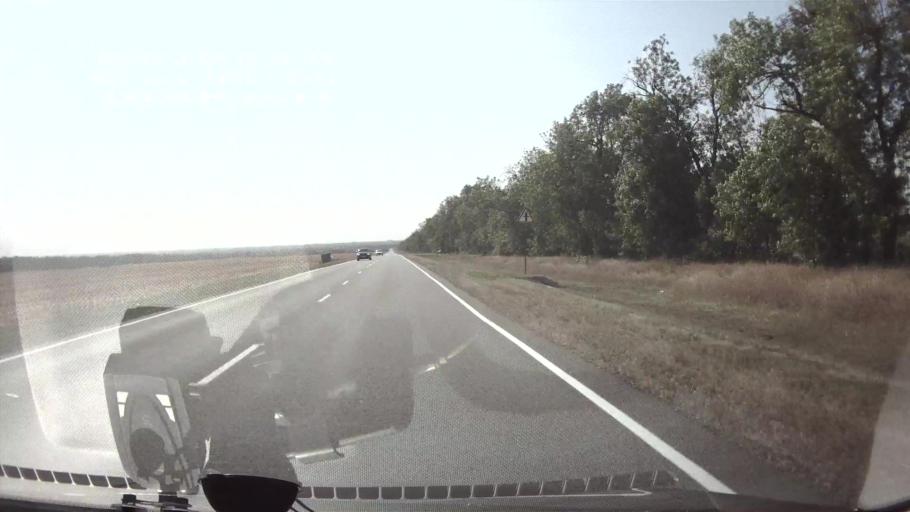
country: RU
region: Krasnodarskiy
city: Dmitriyevskaya
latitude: 45.7689
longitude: 40.7194
